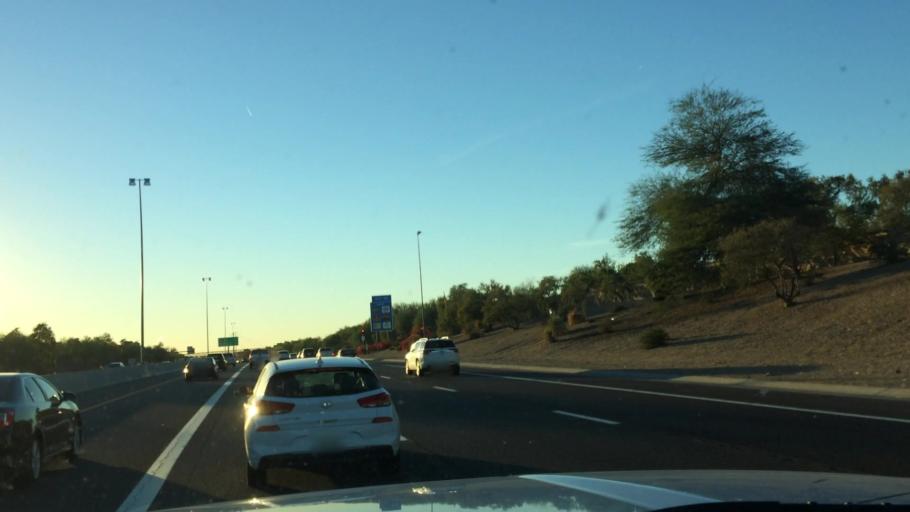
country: US
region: Arizona
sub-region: Maricopa County
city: Peoria
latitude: 33.6657
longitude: -112.1892
